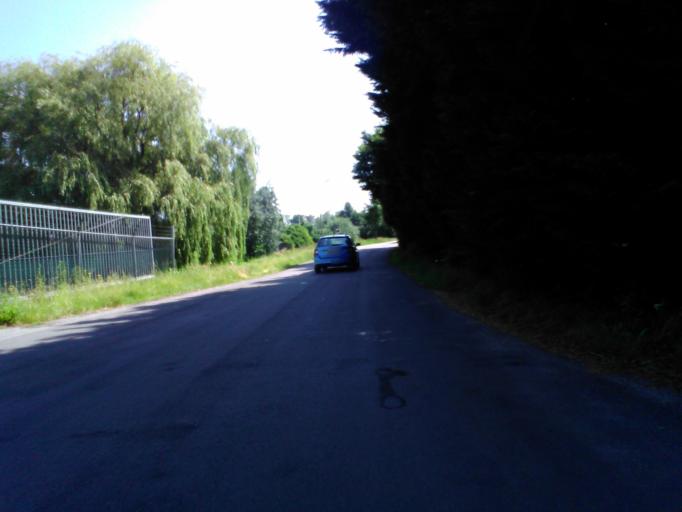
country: NL
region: South Holland
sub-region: Gemeente Boskoop
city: Boskoop
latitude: 52.0897
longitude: 4.6468
